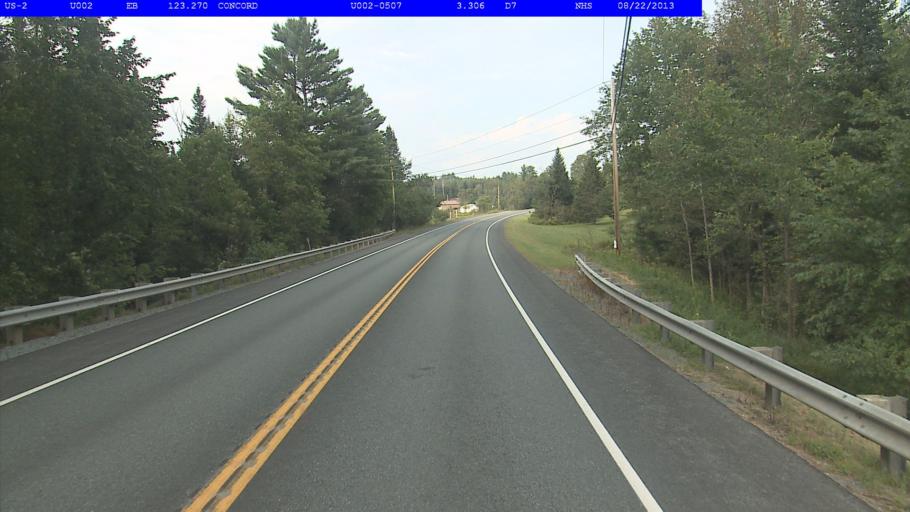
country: US
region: Vermont
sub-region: Caledonia County
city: St Johnsbury
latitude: 44.4420
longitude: -71.8784
